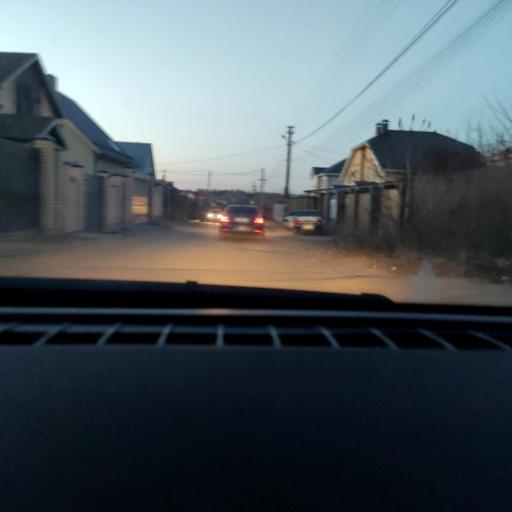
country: RU
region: Voronezj
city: Podgornoye
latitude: 51.7437
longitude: 39.1621
